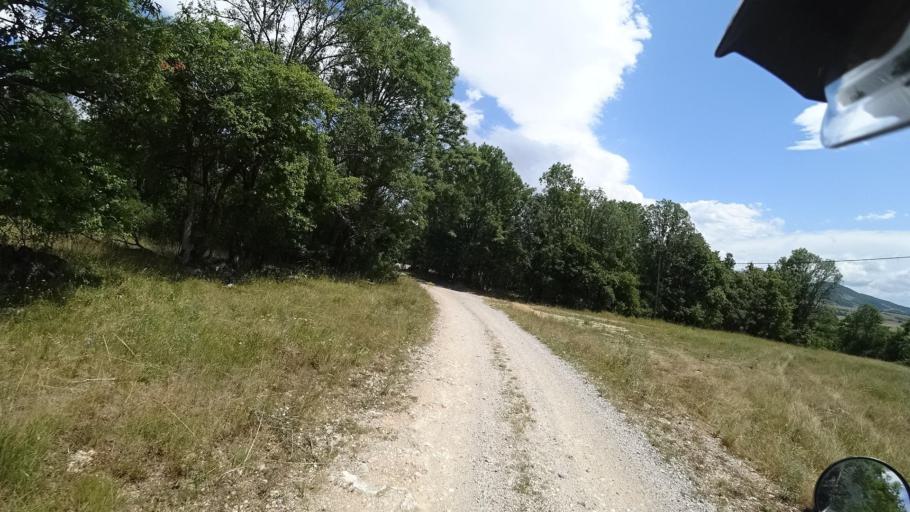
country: HR
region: Licko-Senjska
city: Gospic
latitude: 44.6172
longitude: 15.6305
